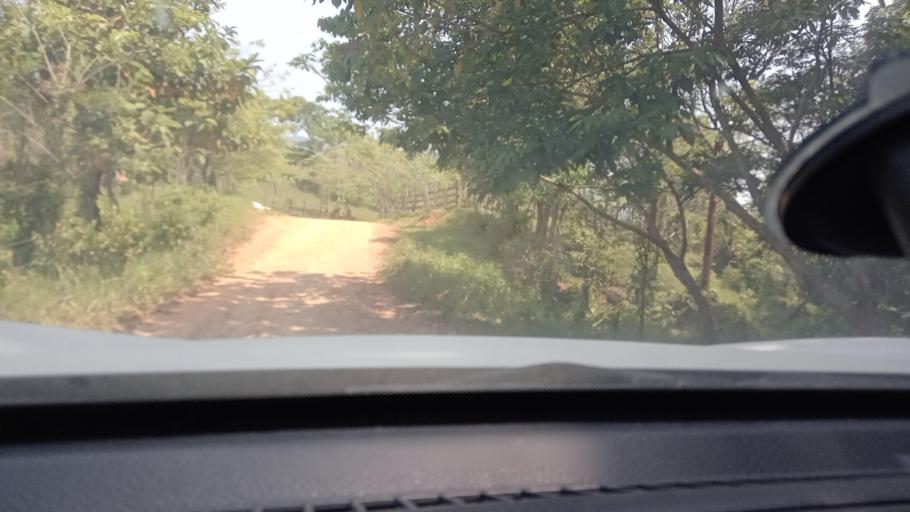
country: MX
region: Tabasco
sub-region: Huimanguillo
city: Francisco Rueda
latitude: 17.4931
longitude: -93.9165
